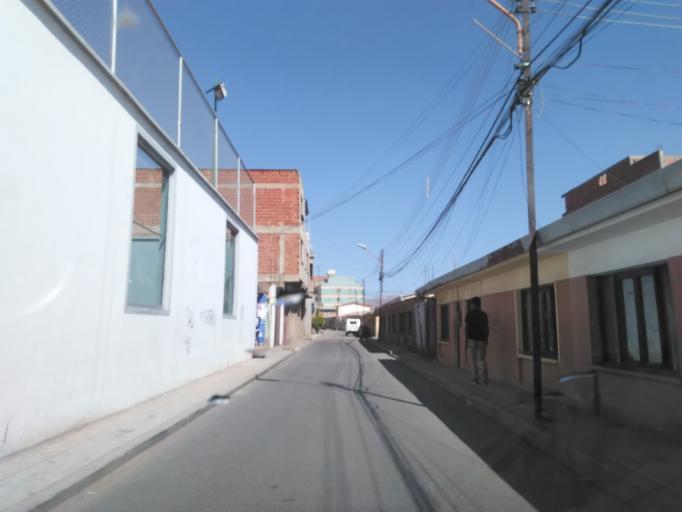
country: BO
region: Cochabamba
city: Cochabamba
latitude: -17.4141
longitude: -66.1550
